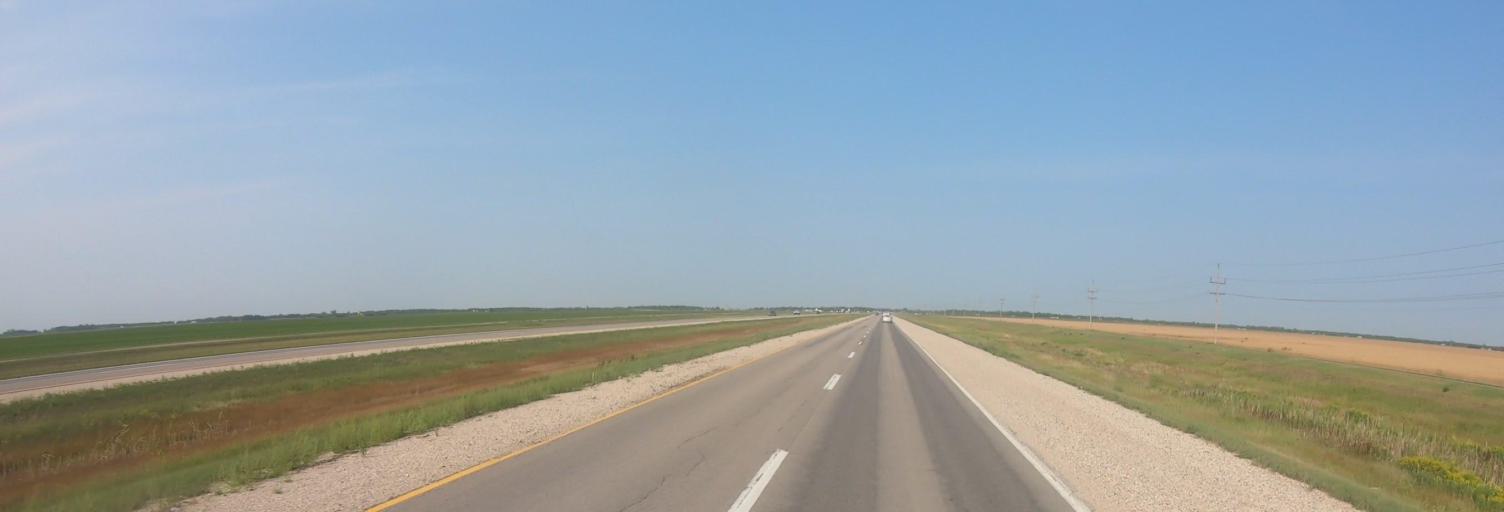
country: CA
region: Manitoba
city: Steinbach
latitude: 49.6465
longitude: -96.6806
